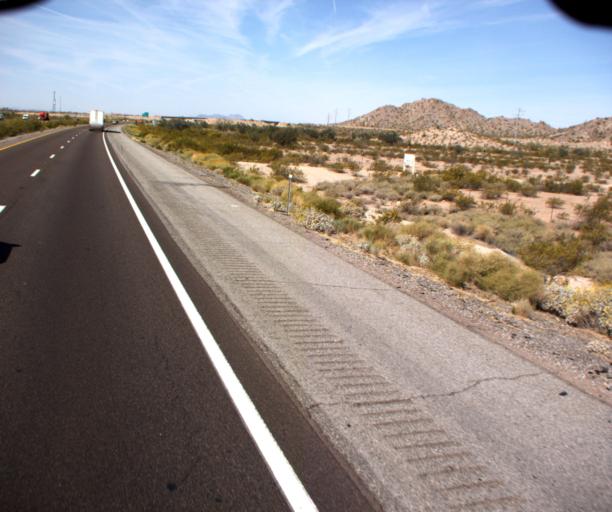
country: US
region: Arizona
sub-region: Maricopa County
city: Buckeye
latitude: 33.4278
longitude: -112.6107
